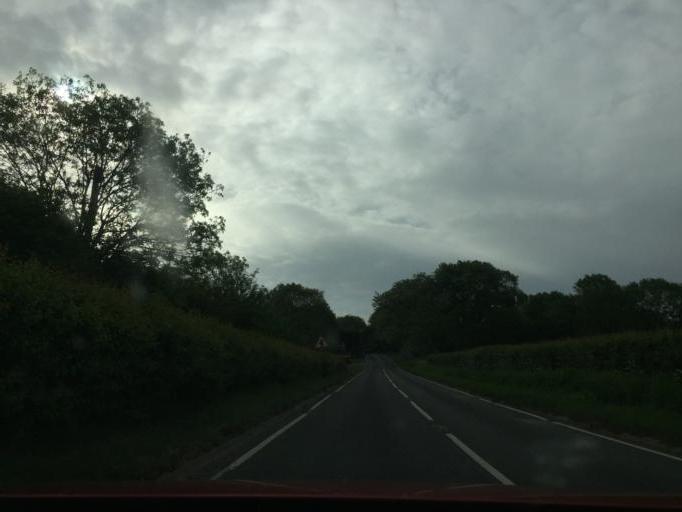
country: GB
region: England
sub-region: Warwickshire
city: Attleborough
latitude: 52.4984
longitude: -1.4095
